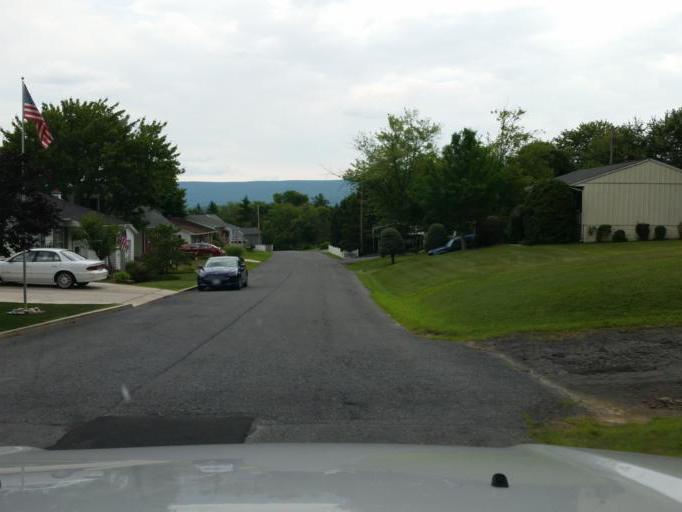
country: US
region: Pennsylvania
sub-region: Blair County
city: Altoona
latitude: 40.5338
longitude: -78.4072
